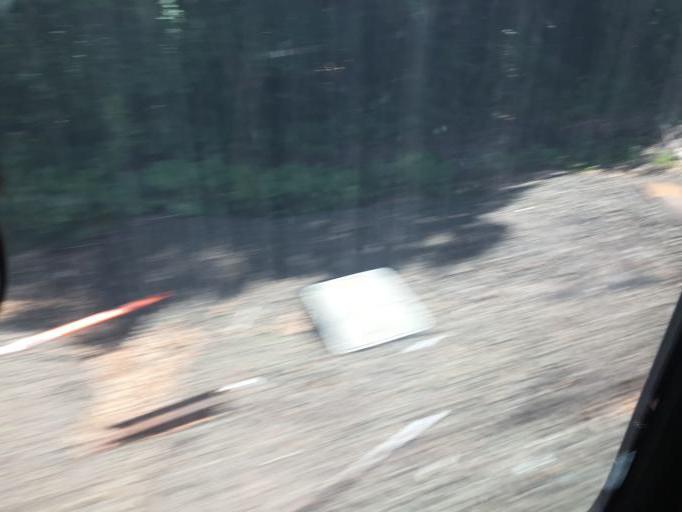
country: US
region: Connecticut
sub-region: New Haven County
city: Meriden
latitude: 41.5177
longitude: -72.8123
